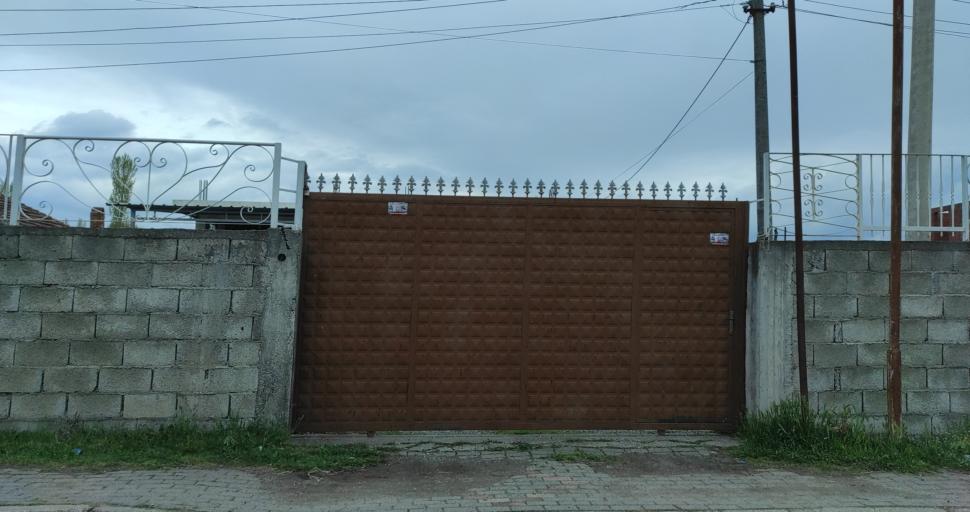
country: AL
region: Shkoder
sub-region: Rrethi i Shkodres
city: Berdica e Madhe
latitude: 41.9810
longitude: 19.4826
